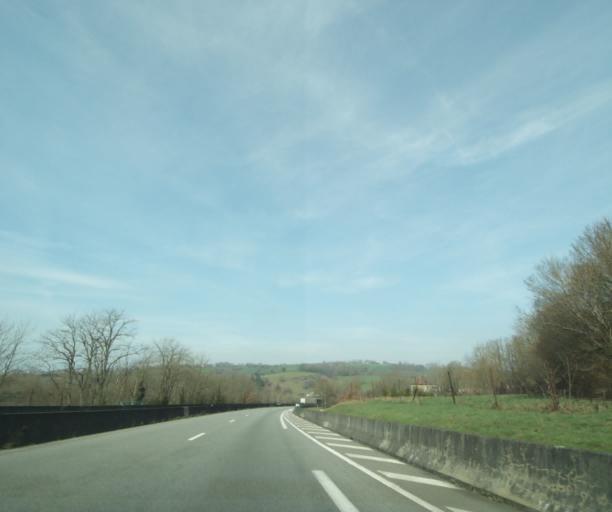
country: FR
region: Limousin
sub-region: Departement de la Haute-Vienne
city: Pierre-Buffiere
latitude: 45.7280
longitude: 1.3419
